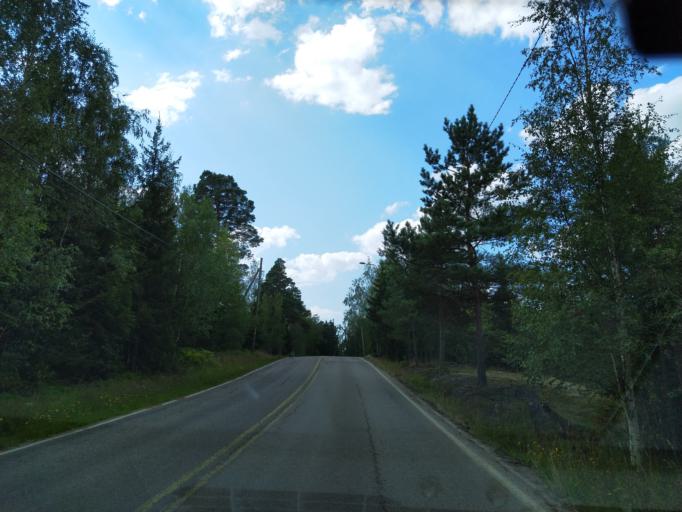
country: FI
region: Uusimaa
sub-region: Helsinki
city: Kirkkonummi
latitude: 60.0452
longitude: 24.4982
